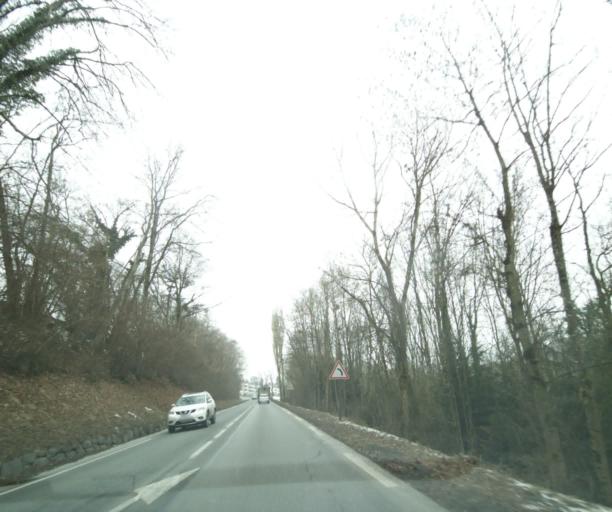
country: FR
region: Rhone-Alpes
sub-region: Departement de la Haute-Savoie
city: Reignier-Esery
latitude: 46.1412
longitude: 6.2693
